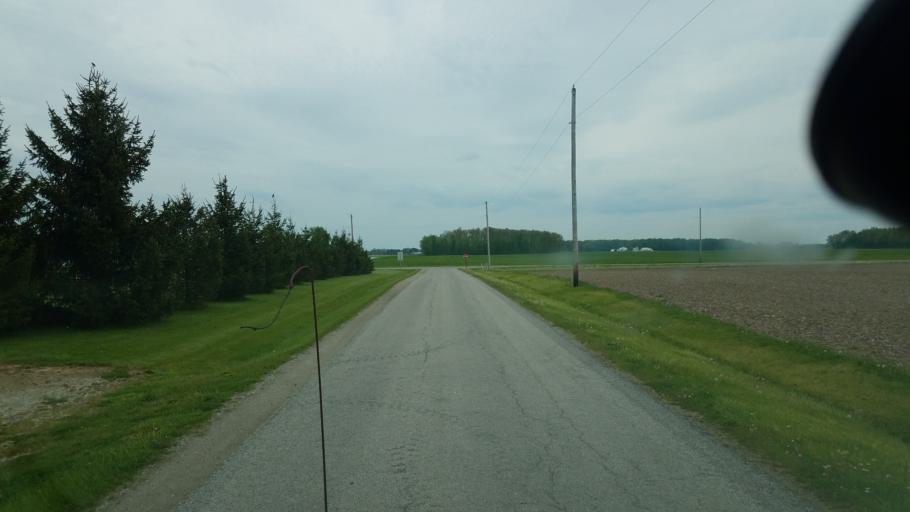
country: US
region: Ohio
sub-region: Huron County
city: Willard
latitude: 41.0116
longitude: -82.7985
